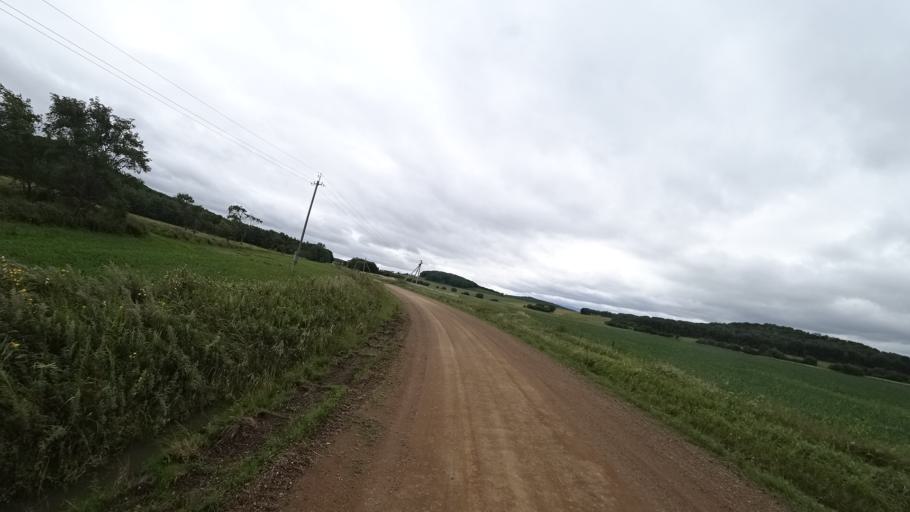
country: RU
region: Primorskiy
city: Chernigovka
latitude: 44.4713
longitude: 132.5816
